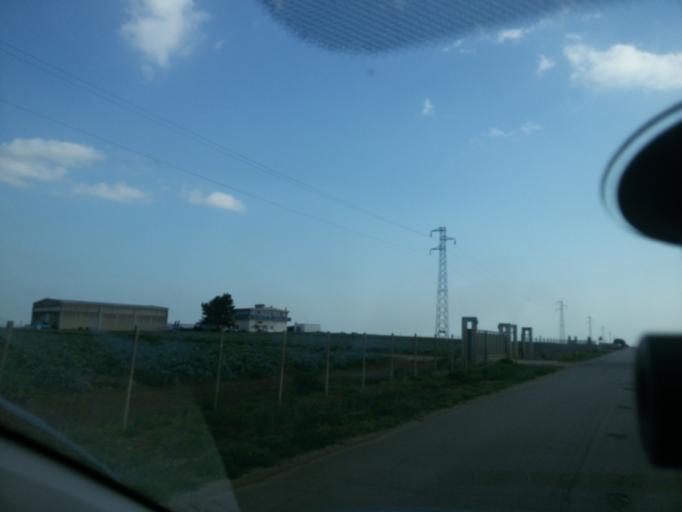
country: IT
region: Apulia
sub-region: Provincia di Brindisi
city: Mesagne
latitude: 40.6403
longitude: 17.8154
